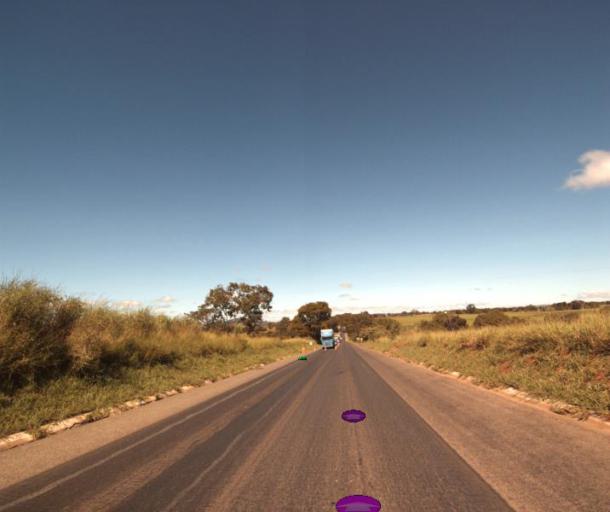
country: BR
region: Goias
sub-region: Itapaci
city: Itapaci
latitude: -15.1119
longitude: -49.4893
